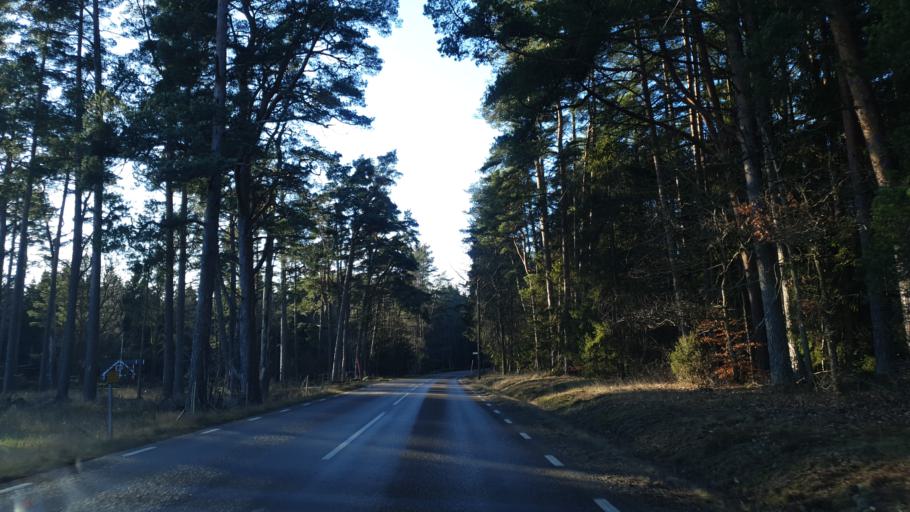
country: SE
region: Blekinge
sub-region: Ronneby Kommun
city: Kallinge
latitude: 56.2175
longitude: 15.3985
